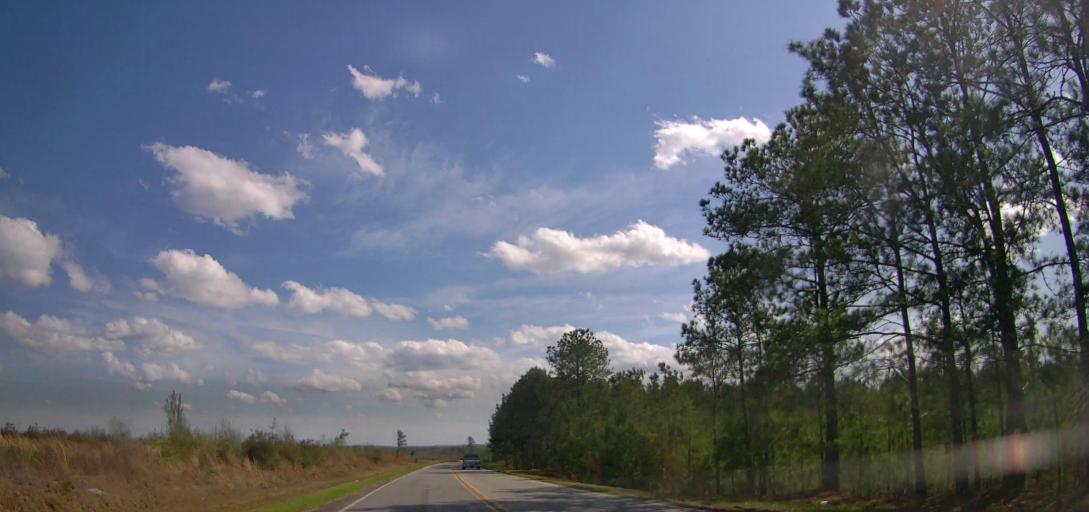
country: US
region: Georgia
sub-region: Wilkinson County
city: Gordon
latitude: 32.9459
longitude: -83.2901
